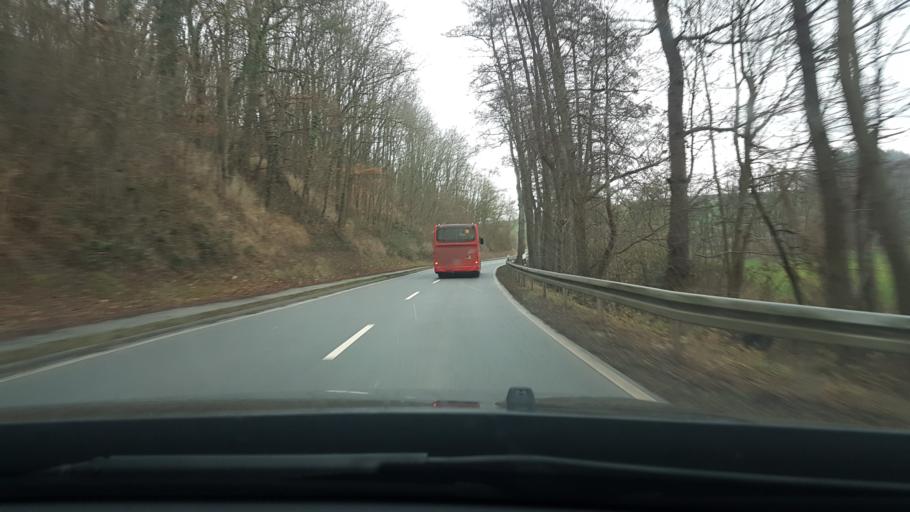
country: DE
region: Hesse
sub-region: Regierungsbezirk Kassel
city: Volkmarsen
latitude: 51.3949
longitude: 9.0733
